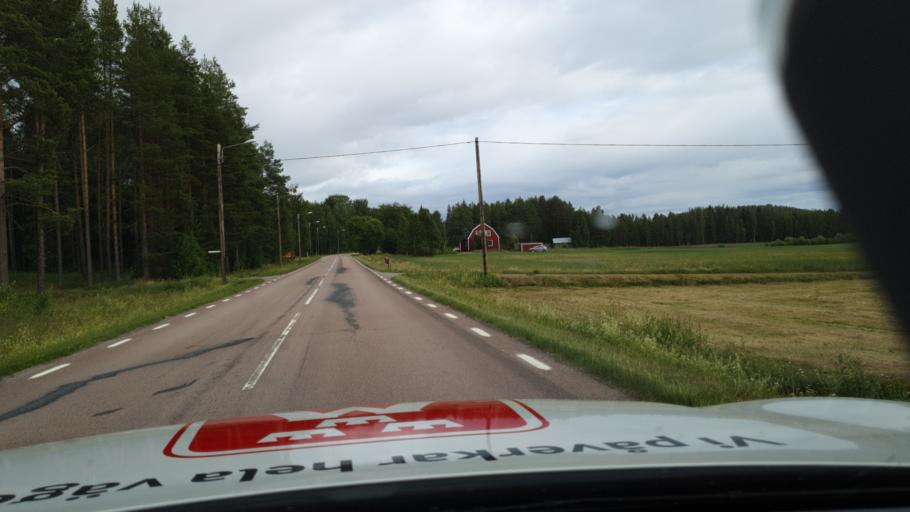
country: SE
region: Jaemtland
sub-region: Stroemsunds Kommun
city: Stroemsund
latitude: 63.7116
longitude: 15.8689
